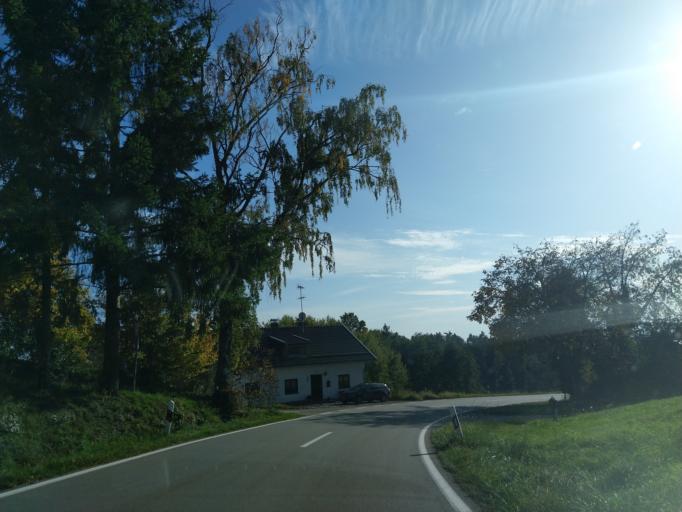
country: DE
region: Bavaria
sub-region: Lower Bavaria
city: Bernried
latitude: 48.9099
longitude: 12.8581
